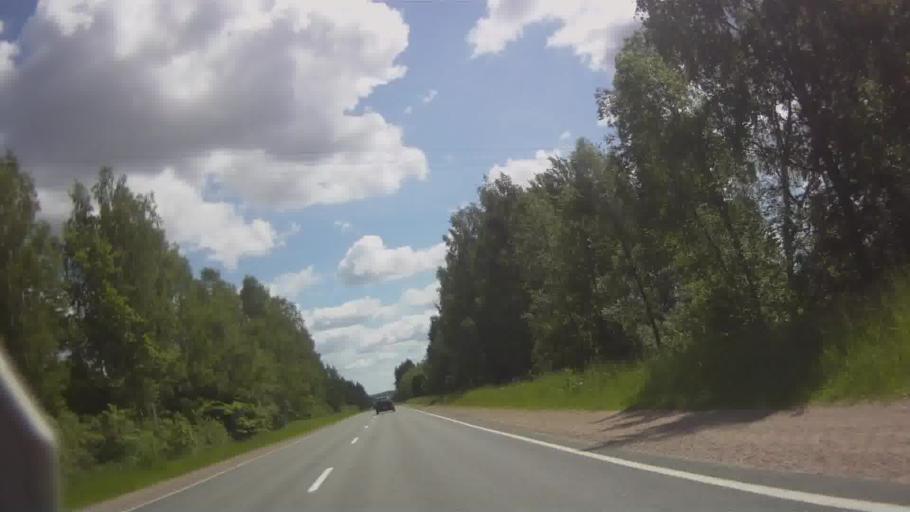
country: LV
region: Varaklani
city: Varaklani
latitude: 56.6077
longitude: 26.8453
